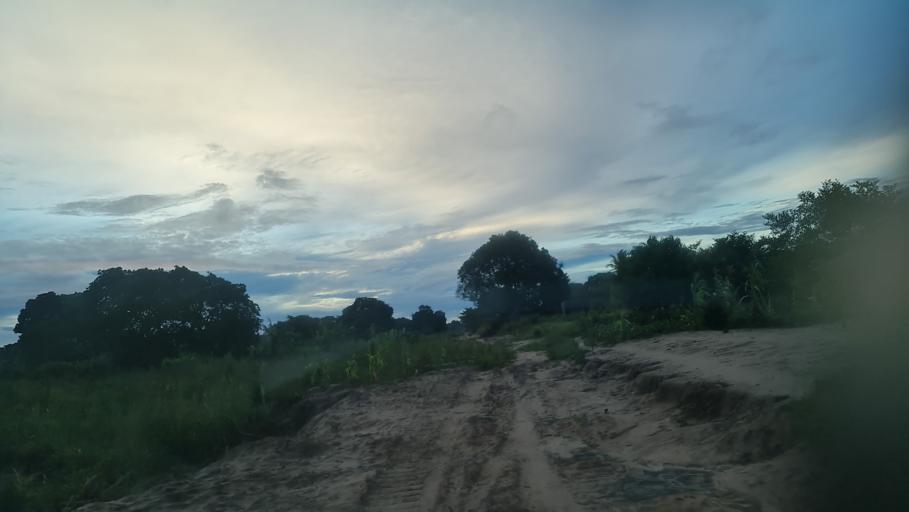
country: MZ
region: Nampula
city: Nampula
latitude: -14.7375
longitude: 39.9277
